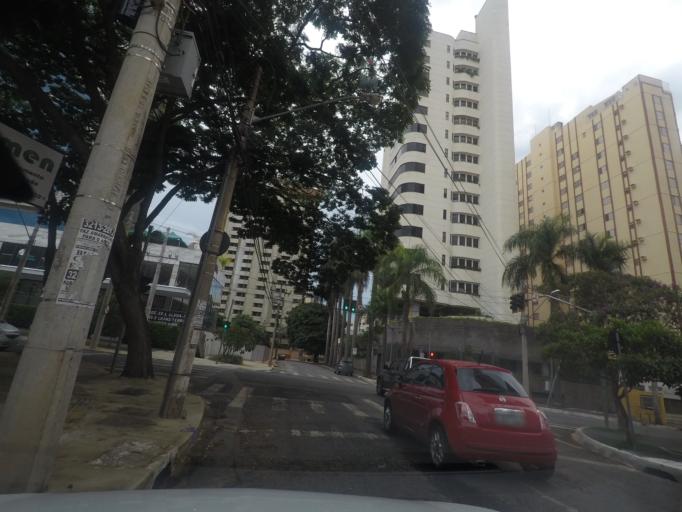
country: BR
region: Goias
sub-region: Goiania
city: Goiania
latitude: -16.6868
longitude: -49.2628
